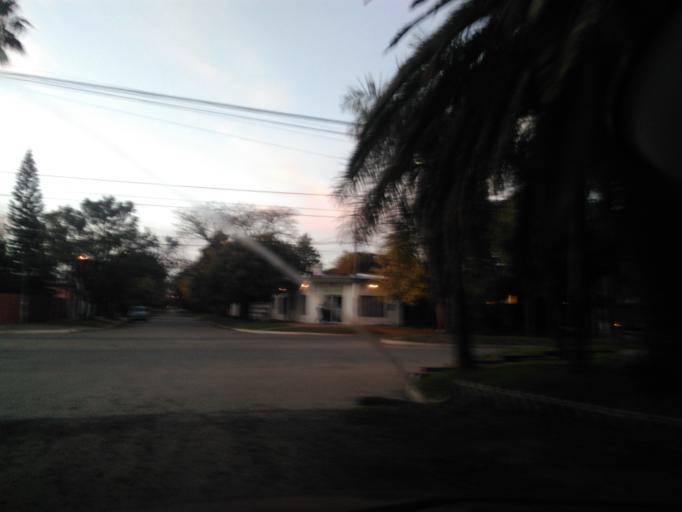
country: AR
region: Chaco
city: Resistencia
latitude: -27.4431
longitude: -58.9692
